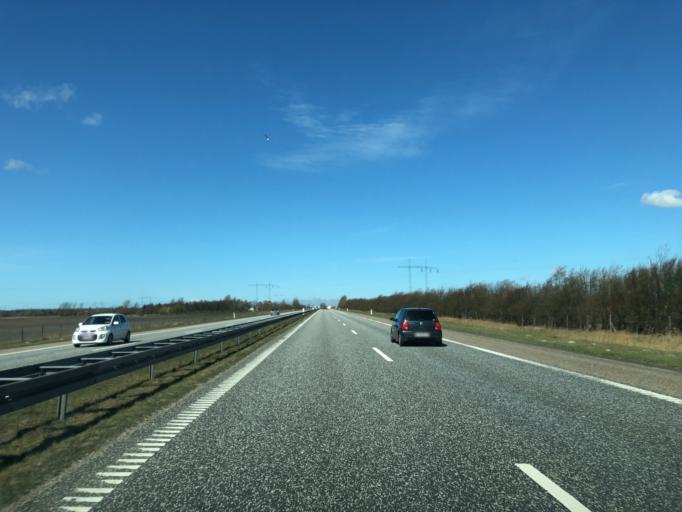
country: DK
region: North Denmark
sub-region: Alborg Kommune
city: Vestbjerg
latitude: 57.1091
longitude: 9.9556
